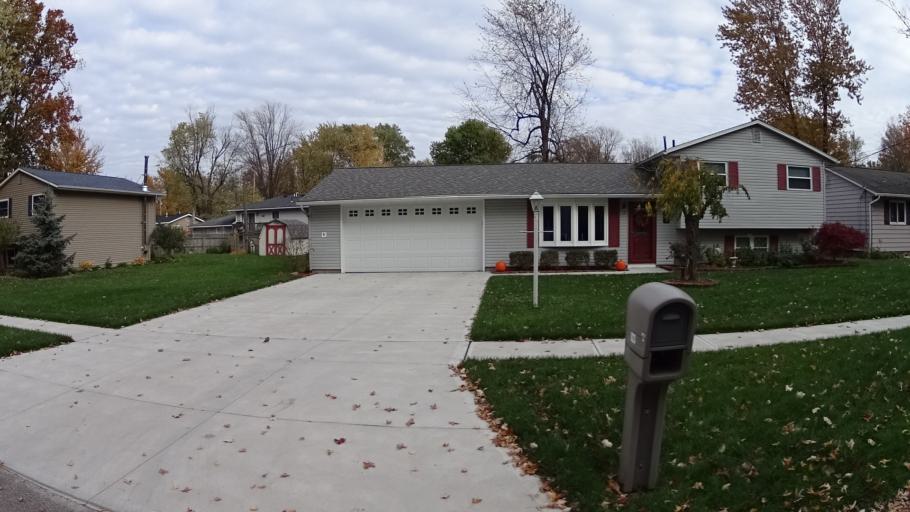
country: US
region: Ohio
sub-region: Lorain County
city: Sheffield Lake
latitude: 41.4843
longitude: -82.1031
